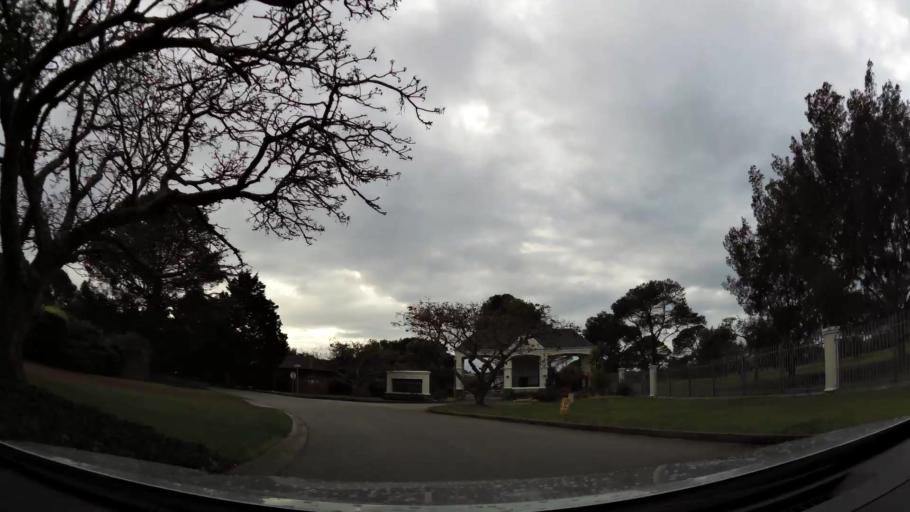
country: ZA
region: Eastern Cape
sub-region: Nelson Mandela Bay Metropolitan Municipality
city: Port Elizabeth
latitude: -33.9763
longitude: 25.5690
